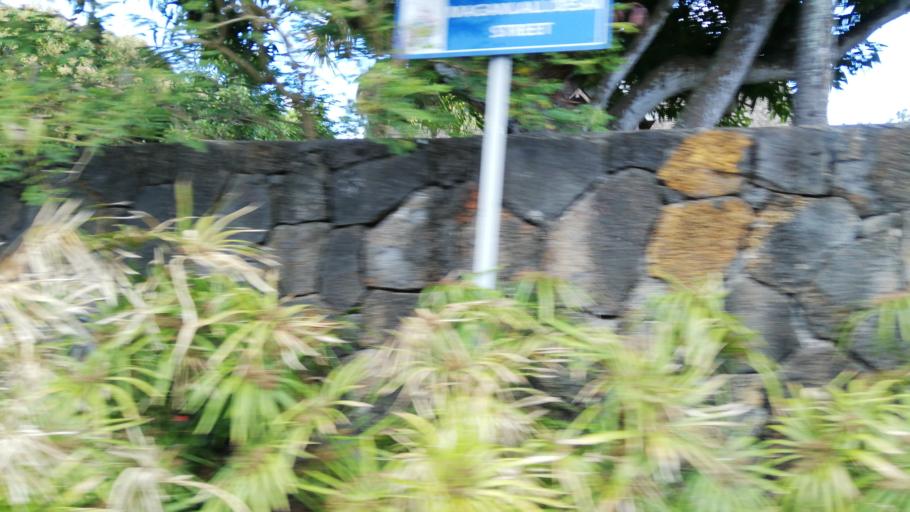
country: MU
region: Moka
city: Moka
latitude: -20.2230
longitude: 57.4737
